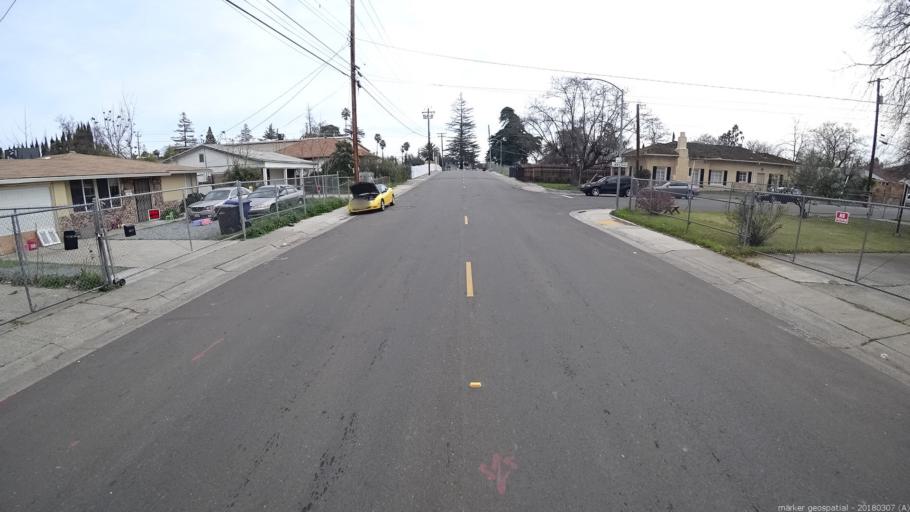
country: US
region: California
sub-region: Sacramento County
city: Parkway
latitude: 38.5353
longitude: -121.4490
